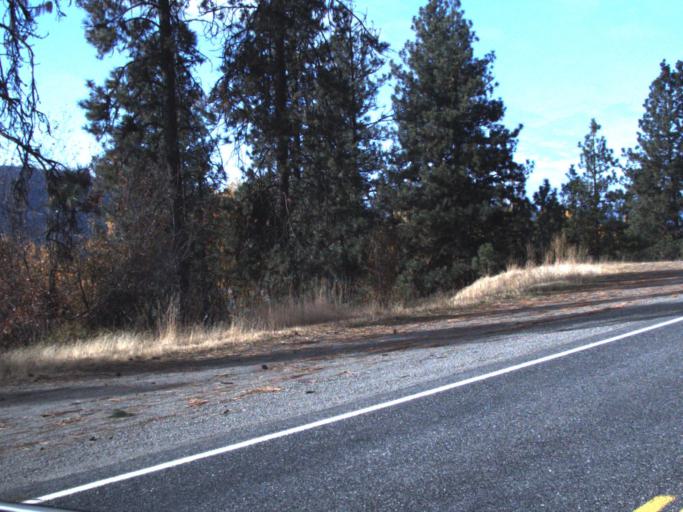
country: US
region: Washington
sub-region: Stevens County
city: Kettle Falls
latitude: 48.3497
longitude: -118.1623
